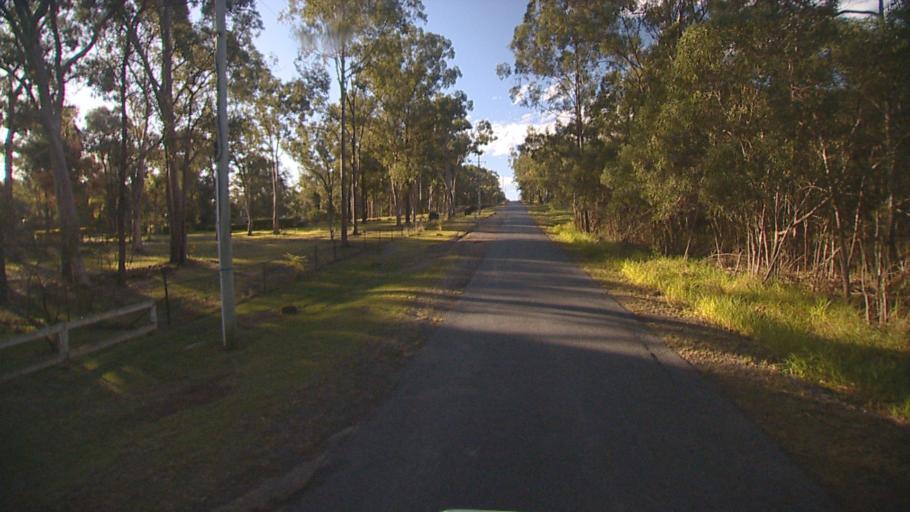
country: AU
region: Queensland
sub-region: Logan
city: Waterford West
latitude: -27.7334
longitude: 153.1516
